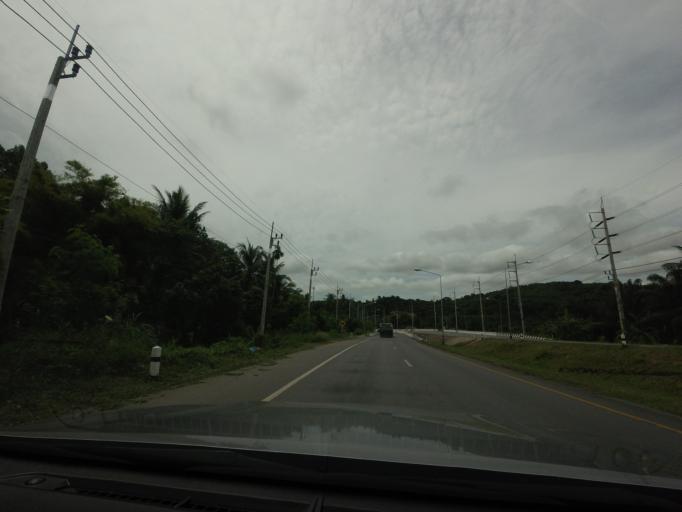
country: TH
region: Nakhon Si Thammarat
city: Hua Sai
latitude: 8.0630
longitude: 100.1980
